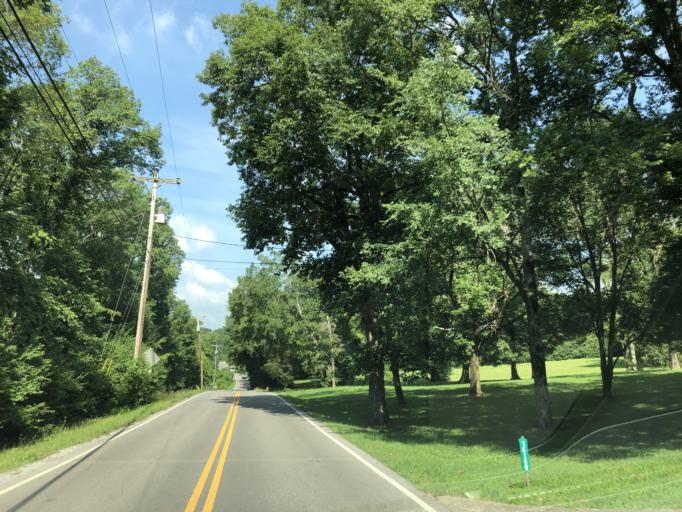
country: US
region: Tennessee
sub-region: Williamson County
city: Nolensville
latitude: 36.0139
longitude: -86.6739
